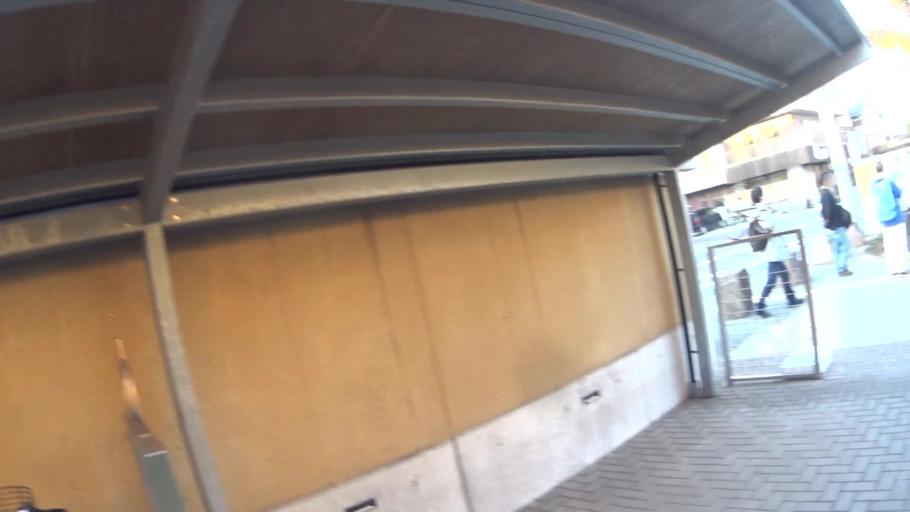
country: JP
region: Saitama
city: Saitama
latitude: 35.9287
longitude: 139.6331
